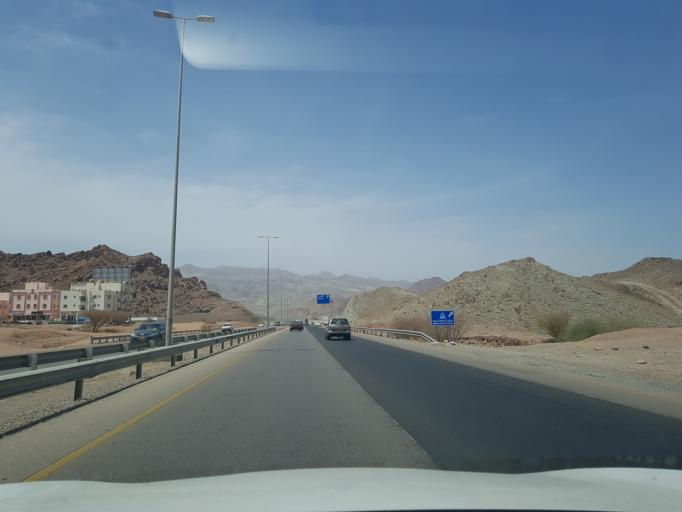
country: OM
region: Muhafazat ad Dakhiliyah
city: Bidbid
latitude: 23.4675
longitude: 58.1377
